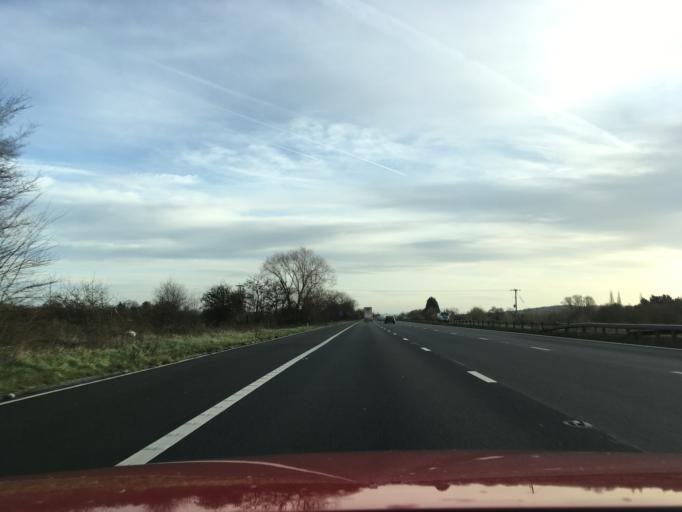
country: GB
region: England
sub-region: Wiltshire
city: Lyneham
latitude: 51.5342
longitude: -2.0089
